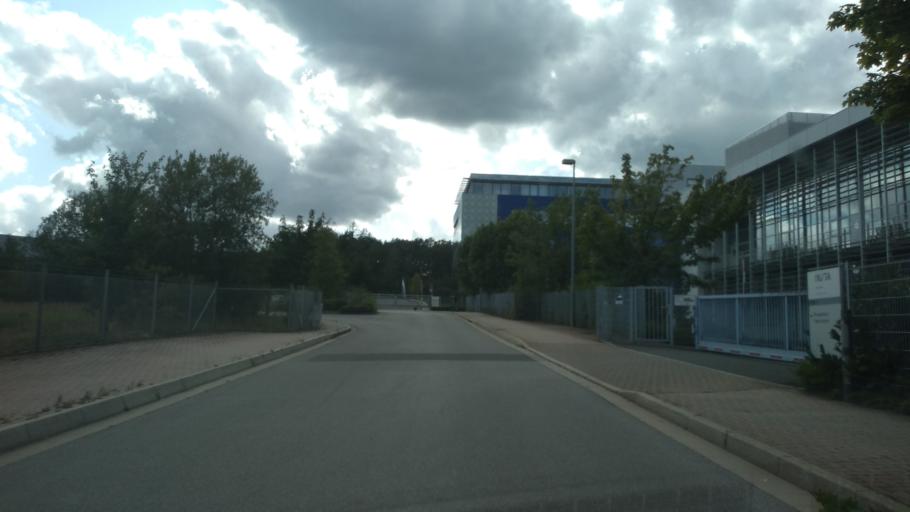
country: DE
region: North Rhine-Westphalia
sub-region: Regierungsbezirk Arnsberg
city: Luedenscheid
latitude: 51.2275
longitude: 7.6001
